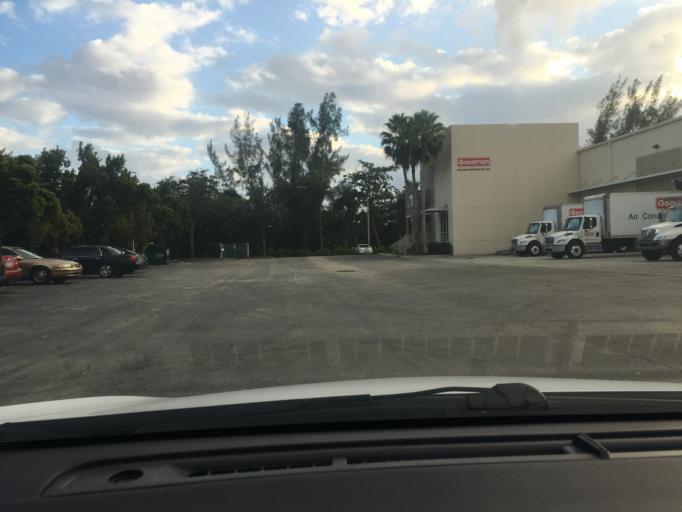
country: US
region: Florida
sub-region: Broward County
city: Dania Beach
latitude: 26.0691
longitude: -80.1788
